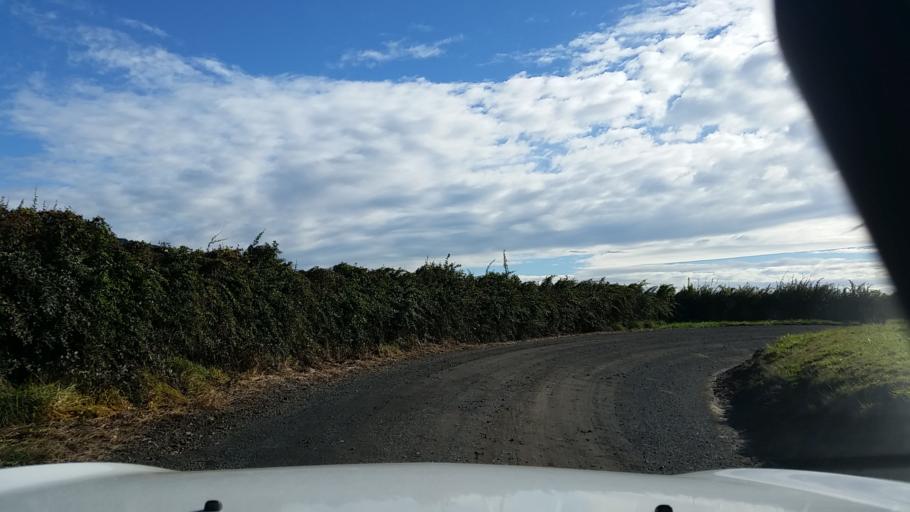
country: NZ
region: Waikato
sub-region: Matamata-Piako District
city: Matamata
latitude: -37.8204
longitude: 175.6431
